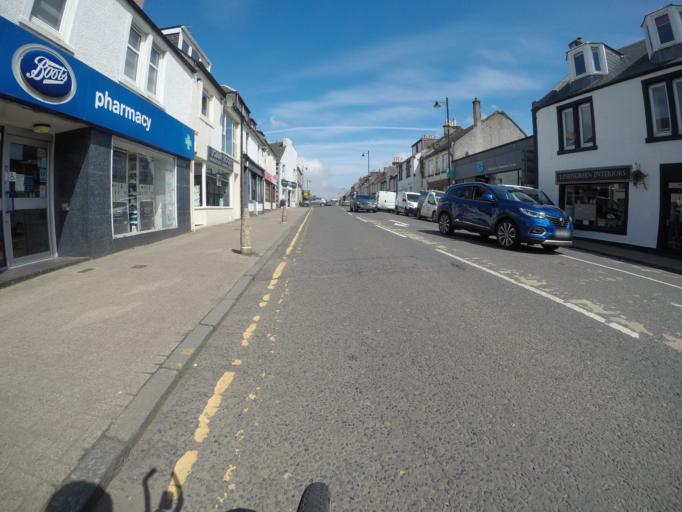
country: GB
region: Scotland
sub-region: East Ayrshire
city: Stewarton
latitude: 55.6804
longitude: -4.5151
